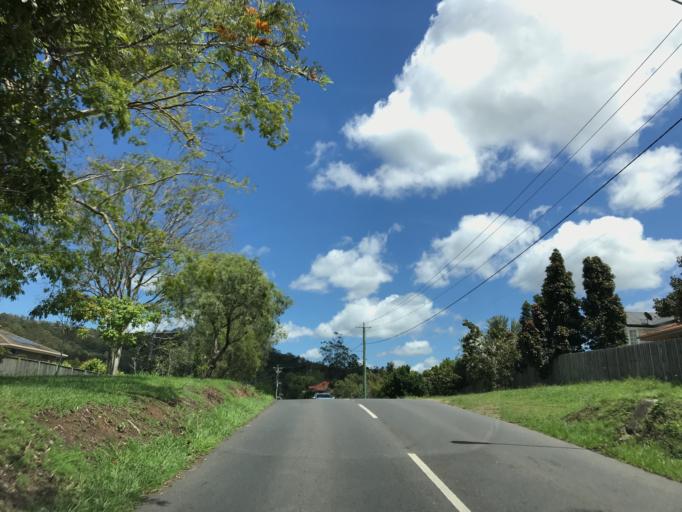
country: AU
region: Queensland
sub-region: Brisbane
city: Kenmore Hills
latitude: -27.4518
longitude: 152.9369
